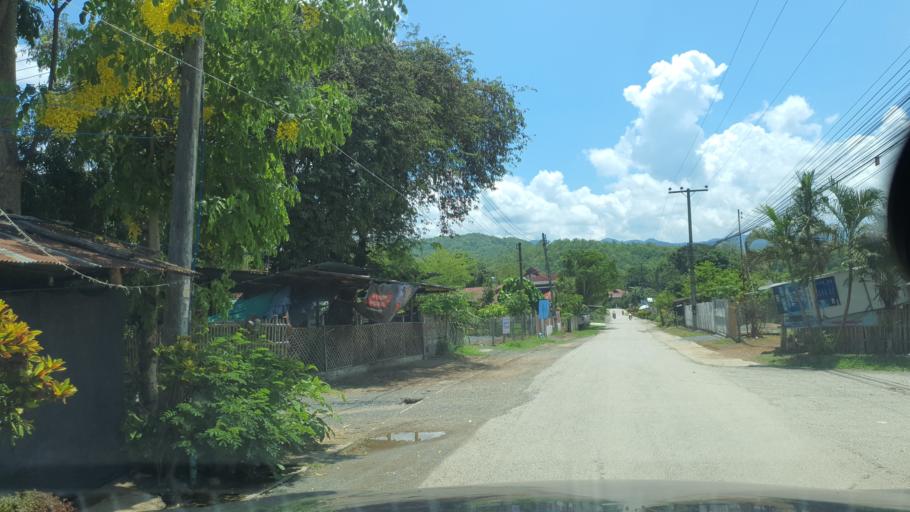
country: TH
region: Chiang Mai
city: Mae On
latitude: 18.8136
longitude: 99.2563
